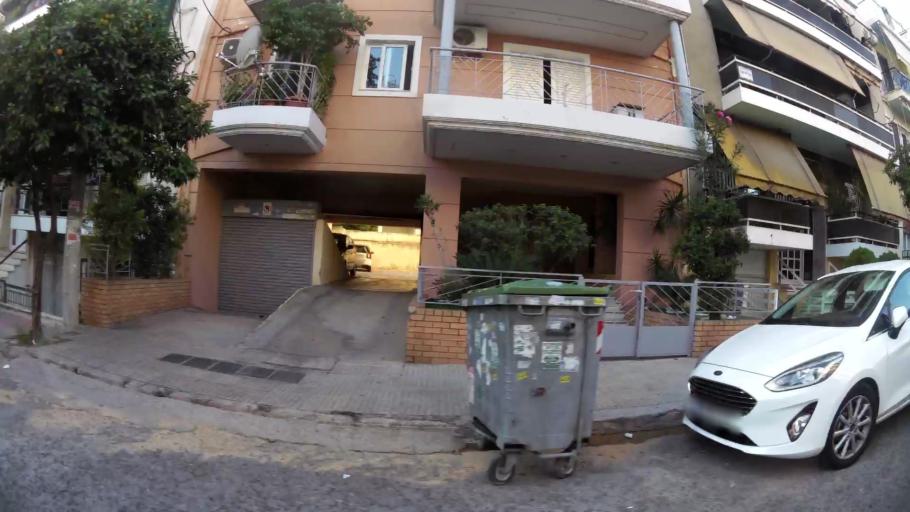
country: GR
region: Attica
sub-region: Nomos Piraios
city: Nikaia
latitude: 37.9674
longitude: 23.6373
